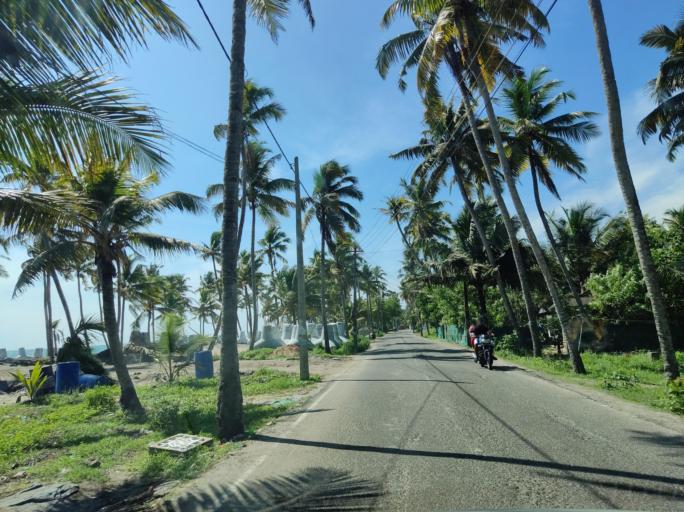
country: IN
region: Kerala
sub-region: Alappuzha
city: Kayankulam
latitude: 9.2408
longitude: 76.4156
